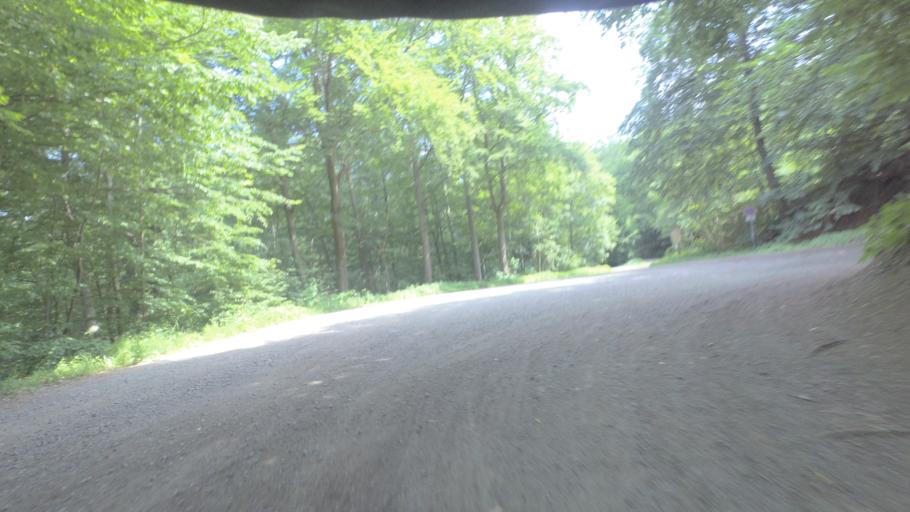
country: DE
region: Lower Saxony
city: Bad Harzburg
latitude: 51.8831
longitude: 10.5940
